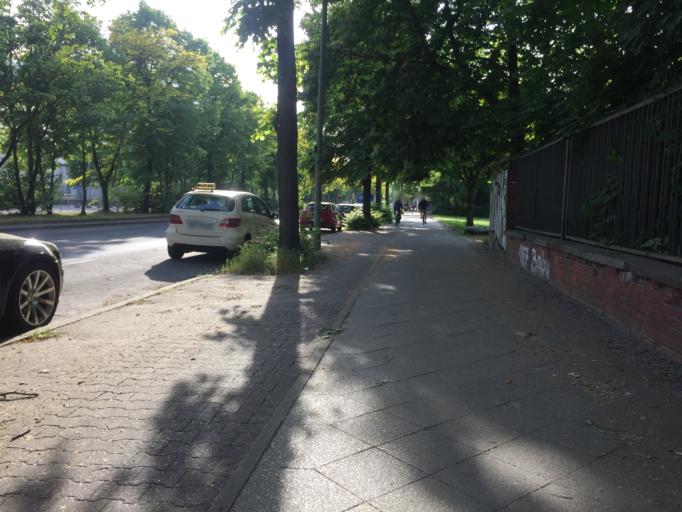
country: DE
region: Berlin
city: Bezirk Kreuzberg
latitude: 52.4934
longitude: 13.4076
